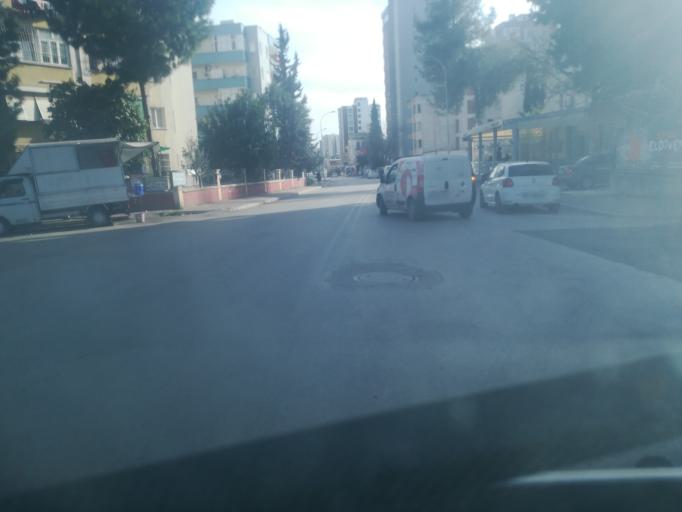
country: TR
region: Adana
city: Adana
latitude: 37.0384
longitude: 35.3127
